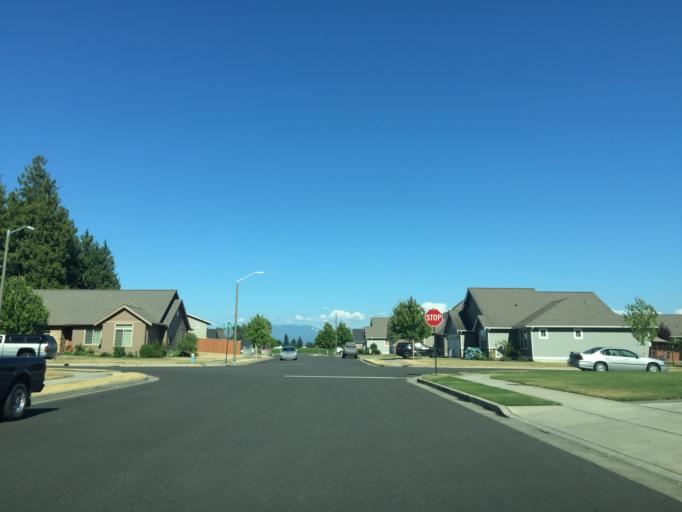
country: US
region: Washington
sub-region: Whatcom County
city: Lynden
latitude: 48.9599
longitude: -122.4214
